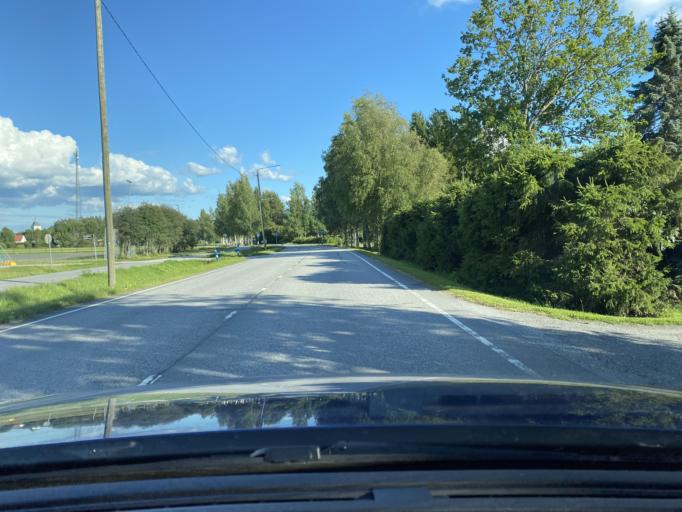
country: FI
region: Ostrobothnia
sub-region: Kyroenmaa
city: Laihia
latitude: 62.9794
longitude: 21.9973
